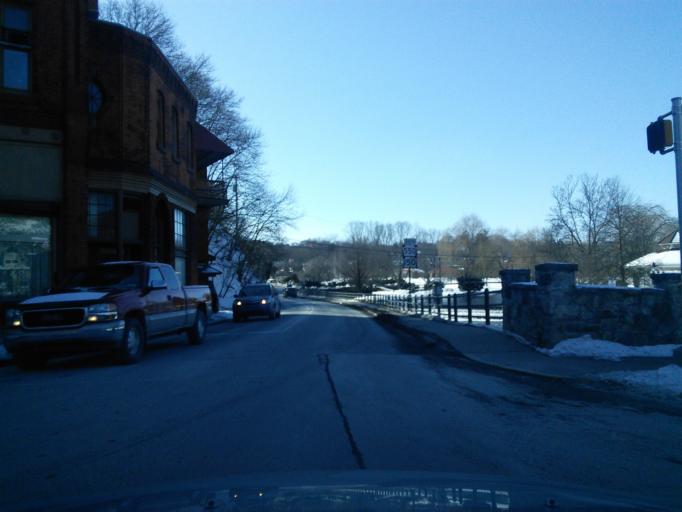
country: US
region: Pennsylvania
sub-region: Centre County
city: Bellefonte
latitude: 40.9115
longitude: -77.7806
